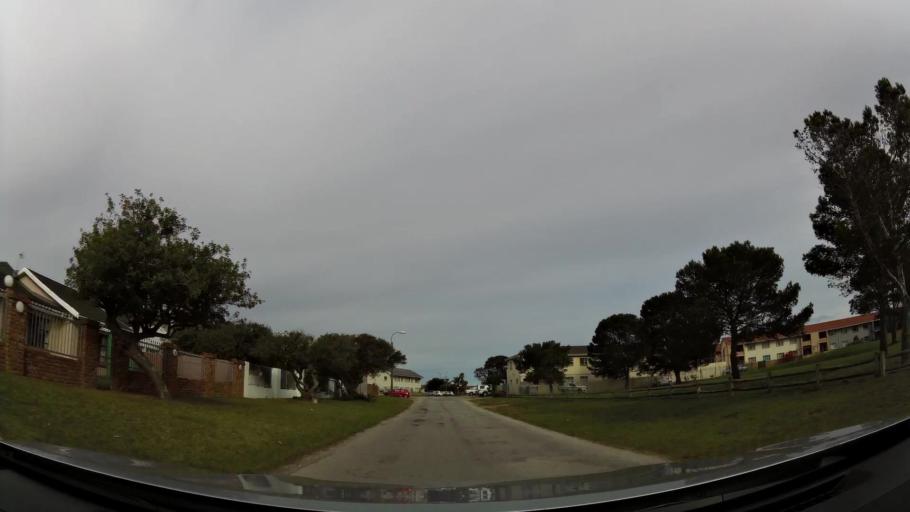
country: ZA
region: Eastern Cape
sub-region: Nelson Mandela Bay Metropolitan Municipality
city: Port Elizabeth
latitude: -33.9391
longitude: 25.4987
